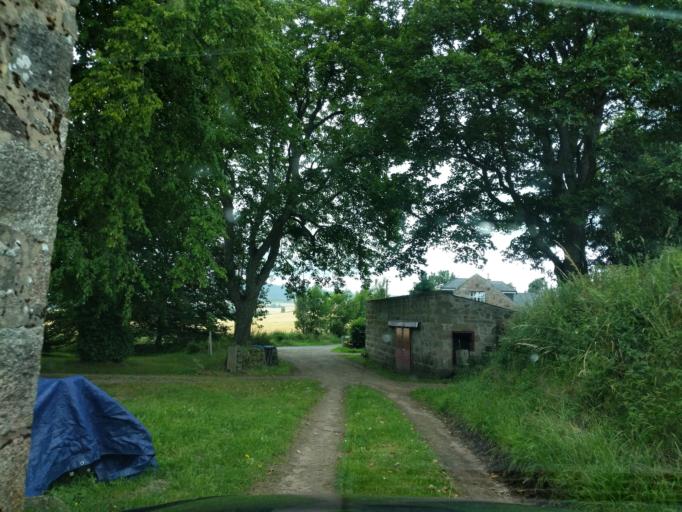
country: GB
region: Scotland
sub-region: Aberdeenshire
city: Aboyne
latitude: 57.1113
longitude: -2.8065
